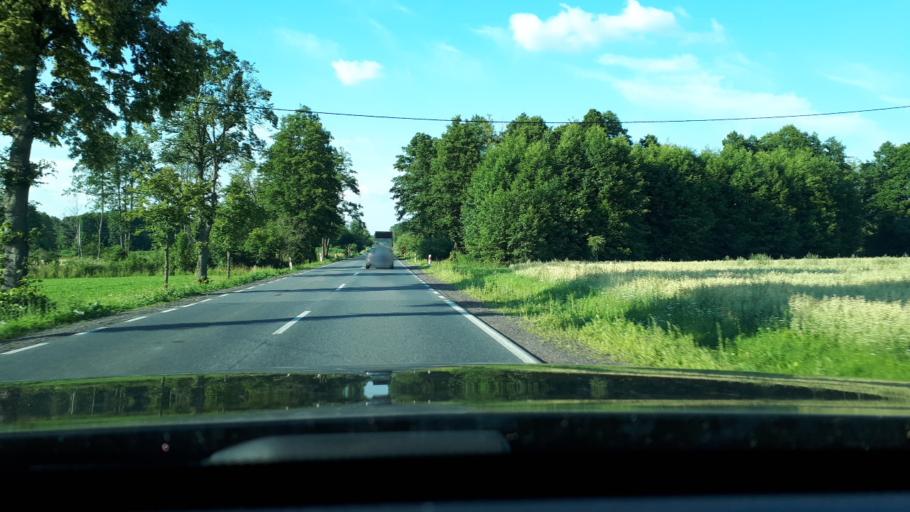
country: PL
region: Masovian Voivodeship
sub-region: Powiat plonski
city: Sochocin
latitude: 52.7210
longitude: 20.5051
